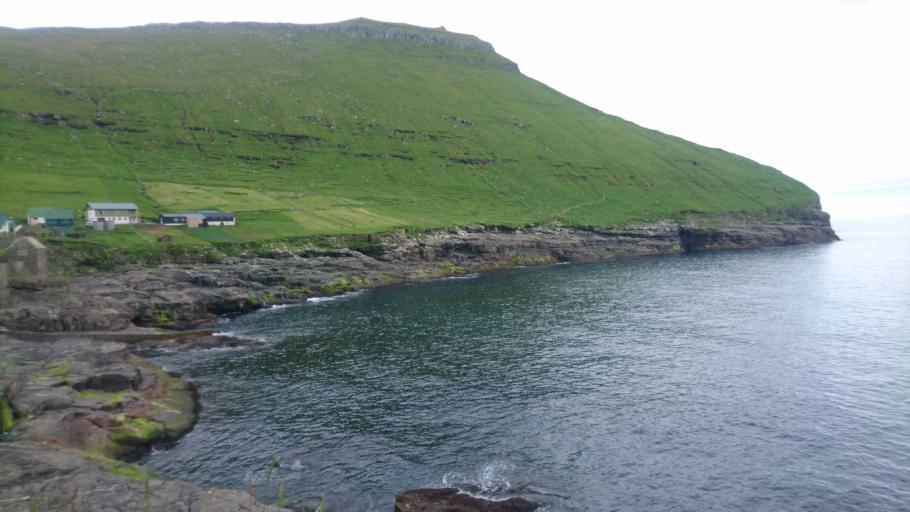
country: FO
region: Nordoyar
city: Klaksvik
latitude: 62.3282
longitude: -6.2766
